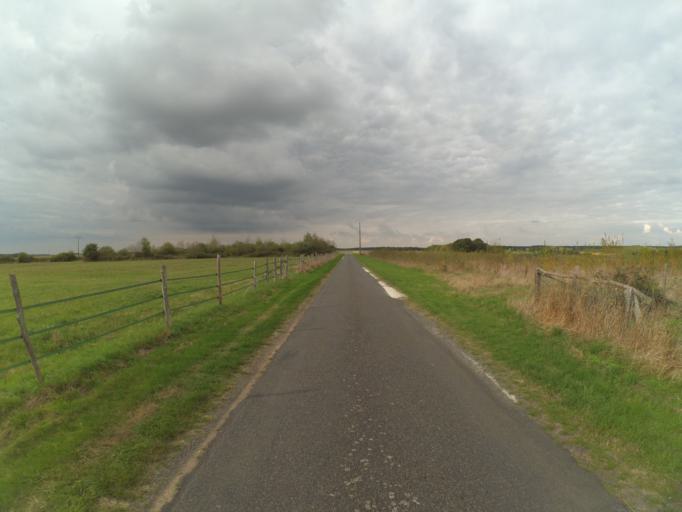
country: FR
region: Centre
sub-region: Departement d'Indre-et-Loire
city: Poce-sur-Cisse
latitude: 47.4874
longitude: 0.9773
